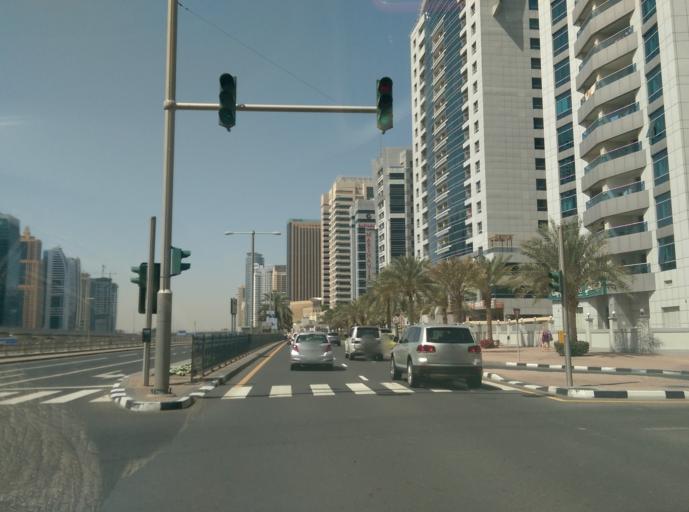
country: AE
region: Dubai
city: Dubai
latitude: 25.0808
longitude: 55.1465
